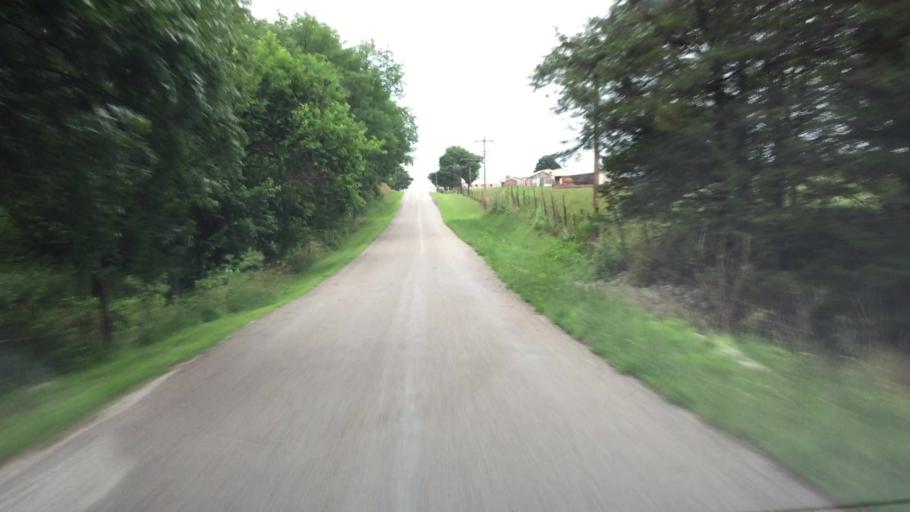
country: US
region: Illinois
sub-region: Hancock County
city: Hamilton
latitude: 40.4263
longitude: -91.3558
